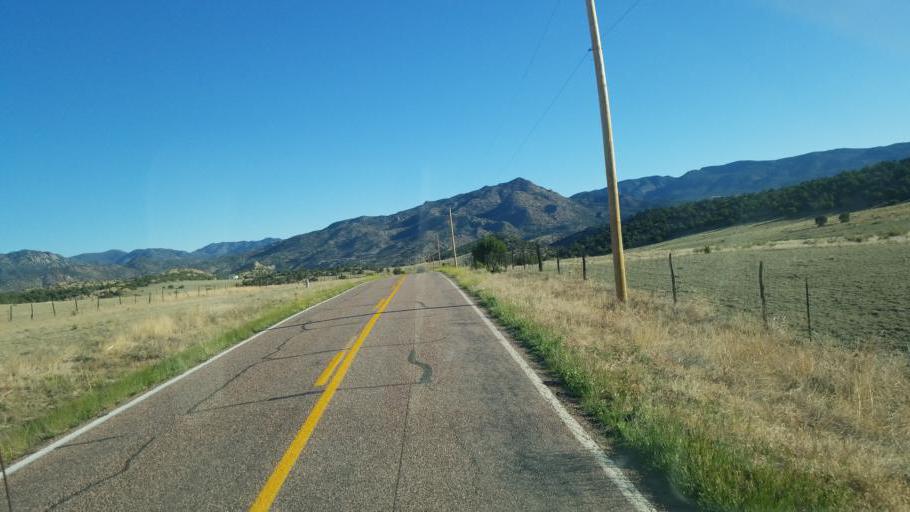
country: US
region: Colorado
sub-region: Fremont County
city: Canon City
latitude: 38.4633
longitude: -105.3765
